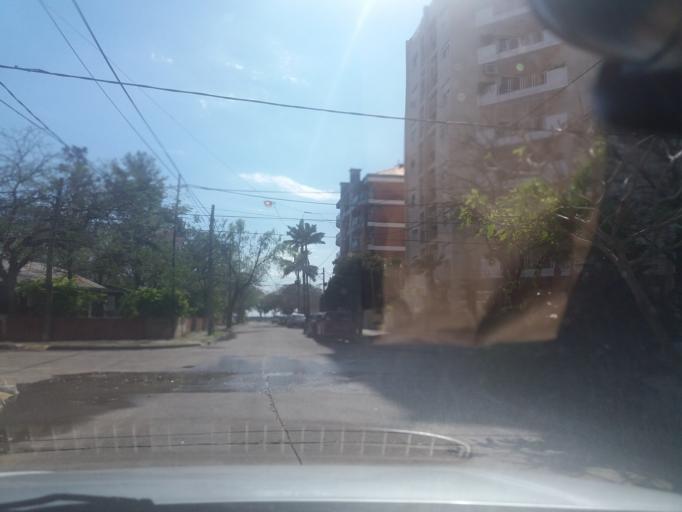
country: AR
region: Corrientes
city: Corrientes
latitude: -27.4678
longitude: -58.8507
